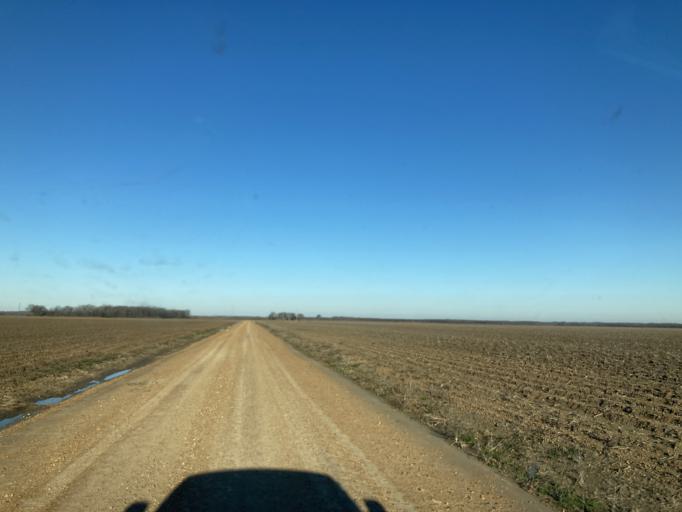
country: US
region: Mississippi
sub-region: Yazoo County
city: Yazoo City
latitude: 32.9228
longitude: -90.6100
